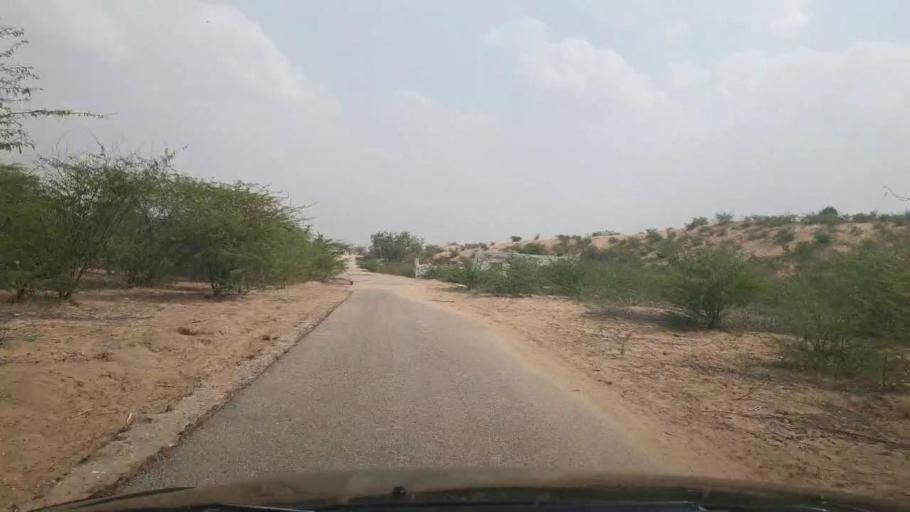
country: PK
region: Sindh
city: Islamkot
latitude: 25.0284
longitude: 70.5475
